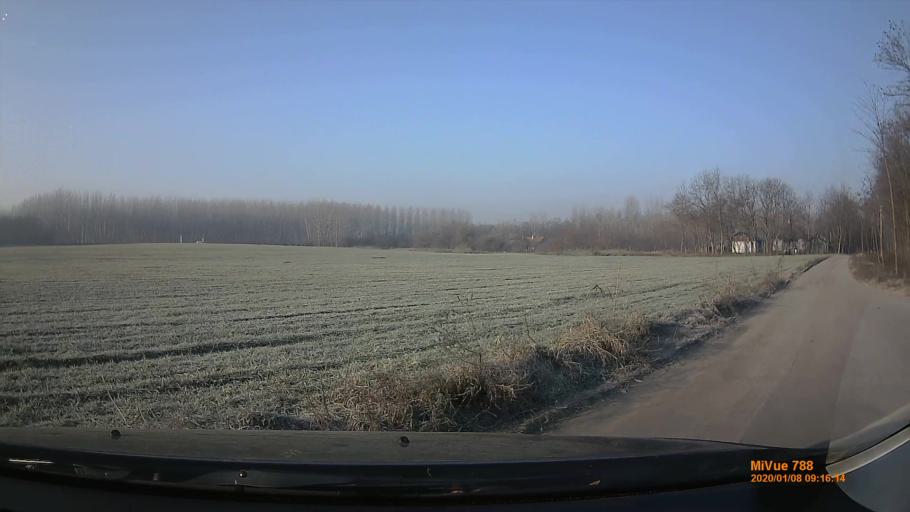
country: HU
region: Bacs-Kiskun
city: Helvecia
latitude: 46.8550
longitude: 19.6605
